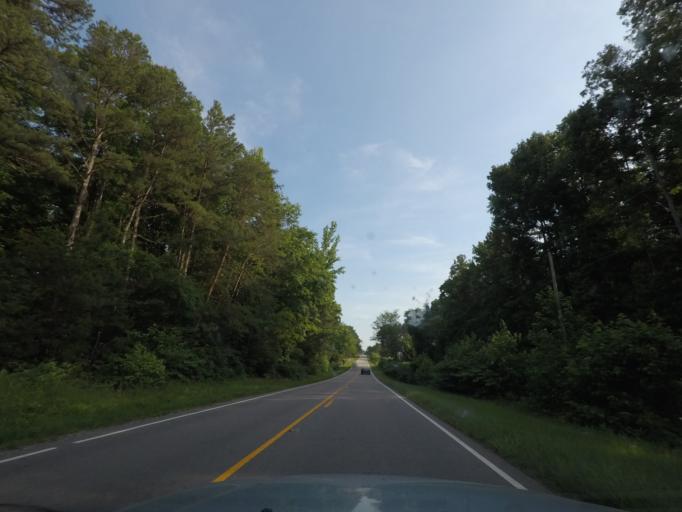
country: US
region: Virginia
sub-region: Mecklenburg County
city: Clarksville
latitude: 36.5147
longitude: -78.5344
